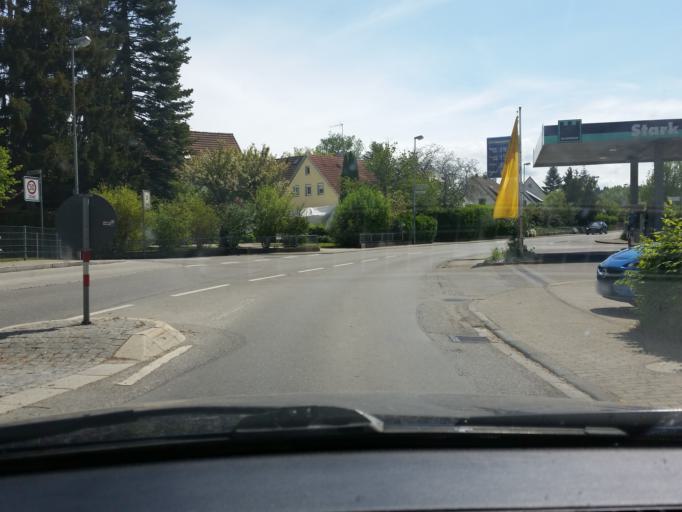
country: DE
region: Baden-Wuerttemberg
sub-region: Freiburg Region
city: Allensbach
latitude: 47.7322
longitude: 9.1181
